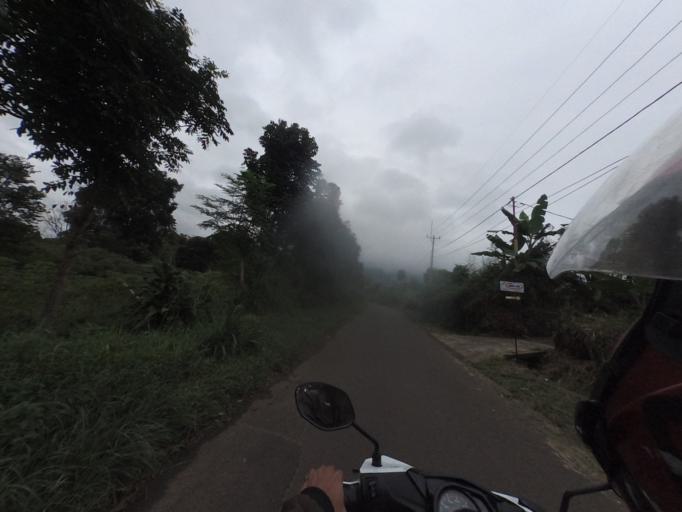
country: ID
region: West Java
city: Bogor
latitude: -6.6521
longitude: 106.7278
